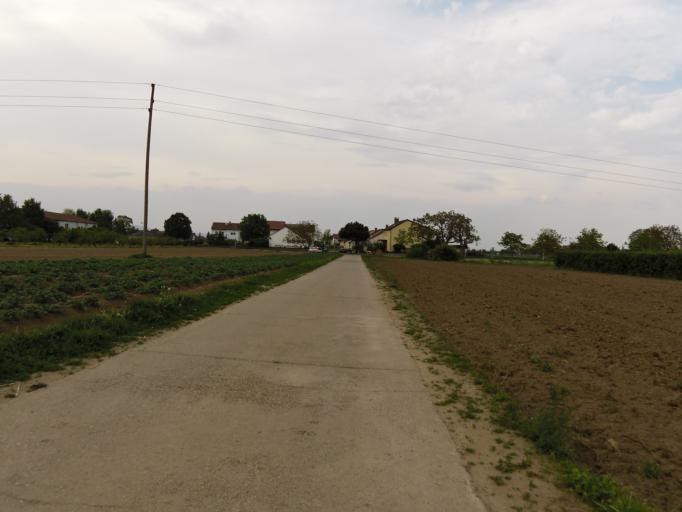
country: DE
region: Rheinland-Pfalz
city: Meckenheim
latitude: 49.4015
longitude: 8.2489
